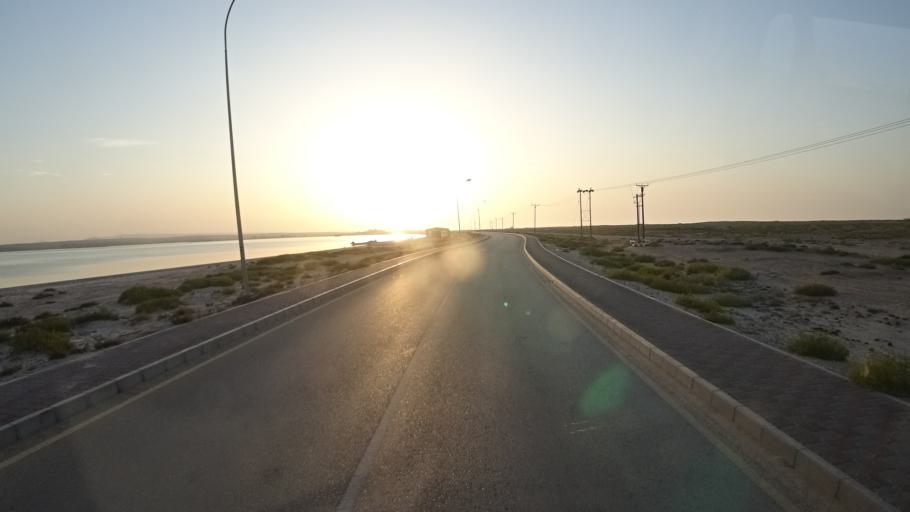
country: OM
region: Ash Sharqiyah
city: Sur
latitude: 22.5274
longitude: 59.7828
